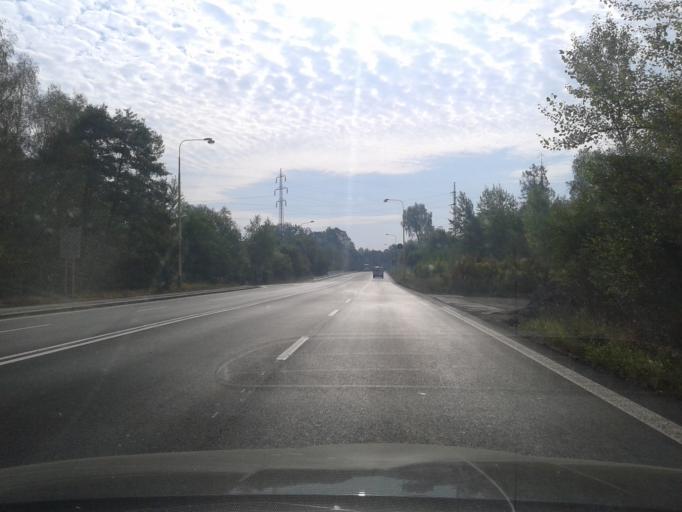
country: CZ
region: Moravskoslezsky
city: Havirov
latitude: 49.8028
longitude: 18.4448
